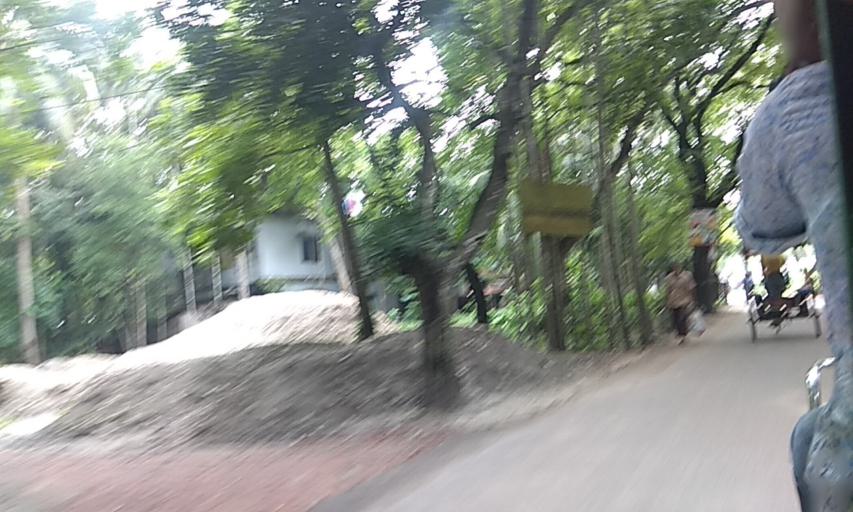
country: BD
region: Dhaka
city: Dohar
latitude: 23.4758
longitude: 90.0286
